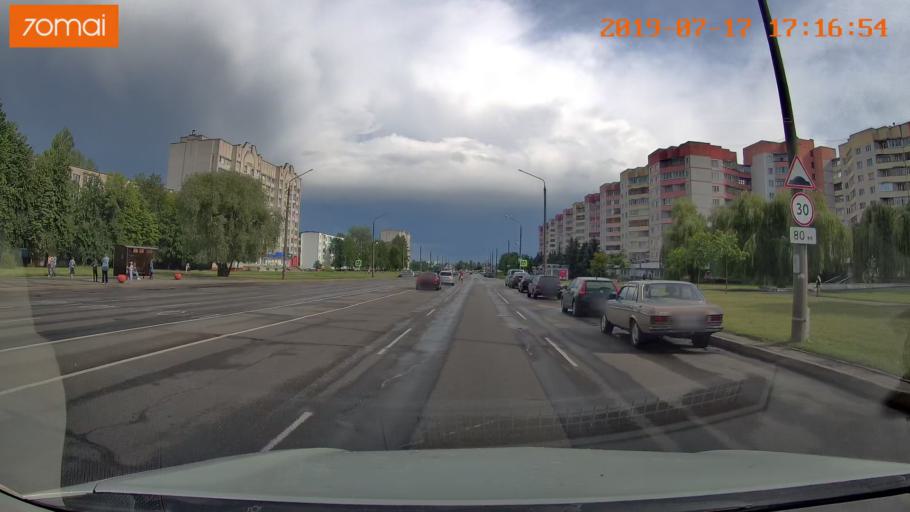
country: BY
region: Mogilev
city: Babruysk
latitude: 53.1645
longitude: 29.1961
